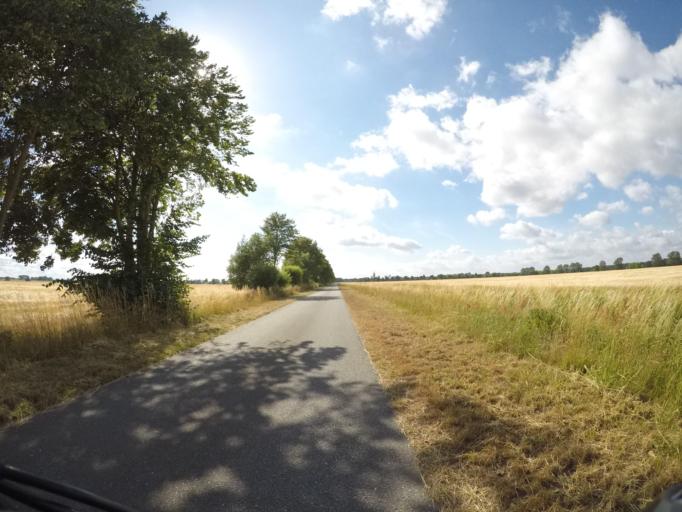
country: DE
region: Lower Saxony
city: Damnatz
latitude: 53.1819
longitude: 11.1651
